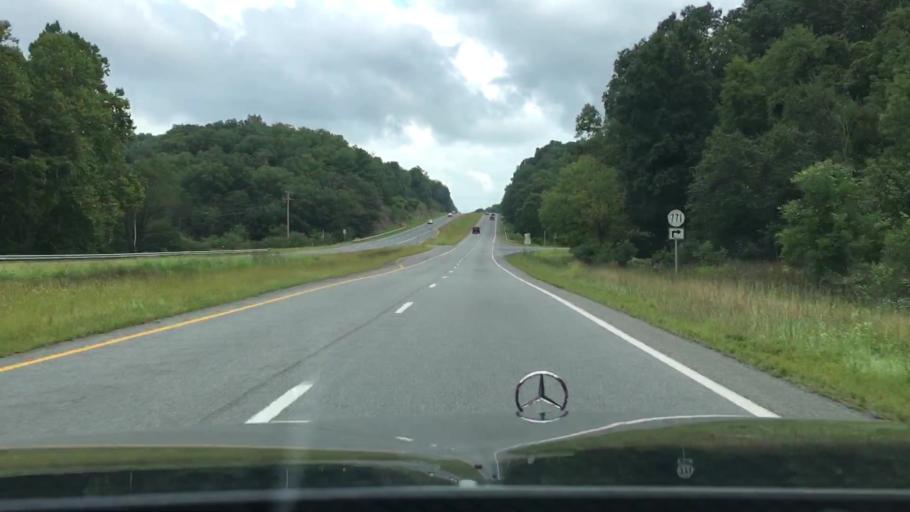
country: US
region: Virginia
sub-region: Frederick County
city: Shawnee Land
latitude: 39.3326
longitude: -78.3072
